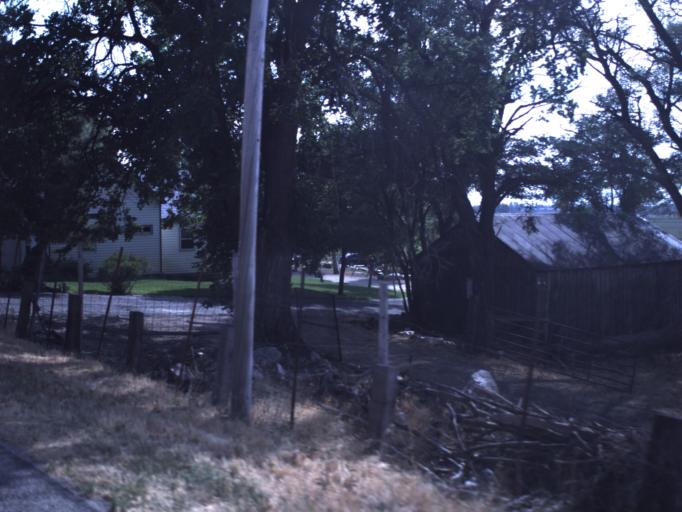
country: US
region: Utah
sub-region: Box Elder County
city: Brigham City
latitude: 41.5438
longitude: -112.0152
